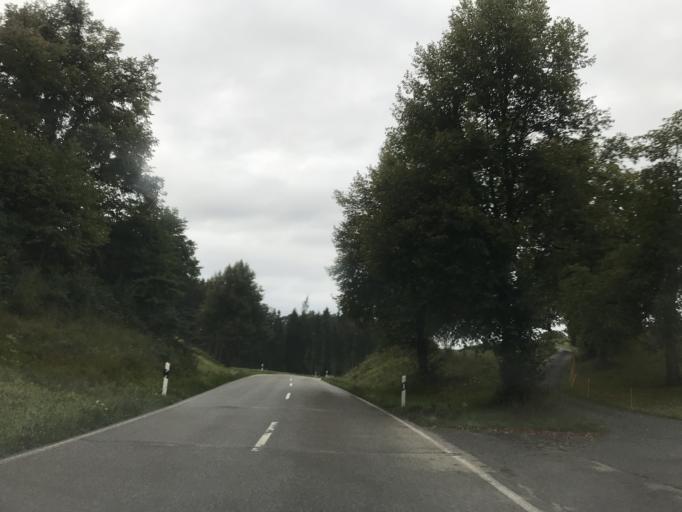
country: DE
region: Baden-Wuerttemberg
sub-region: Freiburg Region
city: Schworstadt
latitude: 47.6201
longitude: 7.8553
